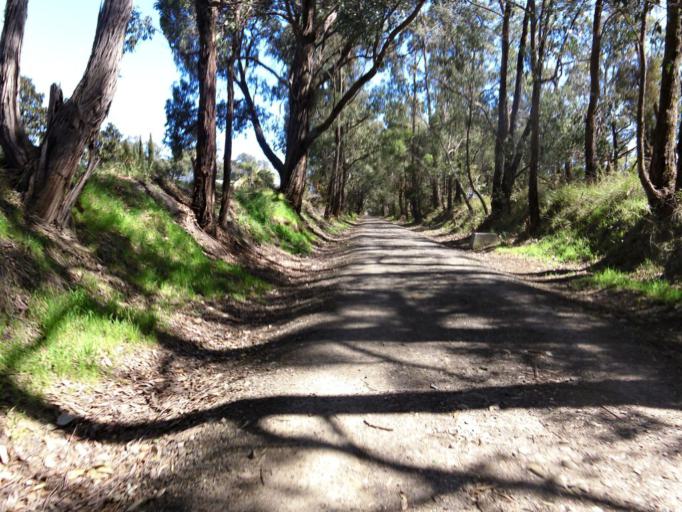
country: AU
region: Victoria
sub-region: Latrobe
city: Moe
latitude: -38.1734
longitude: 146.2815
